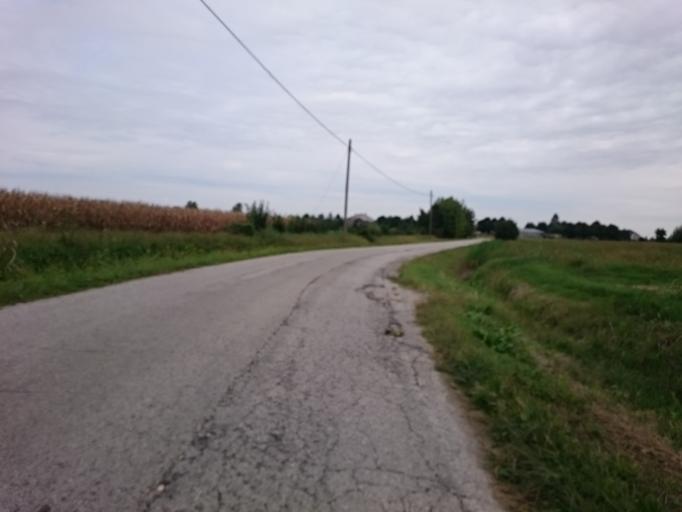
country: IT
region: Veneto
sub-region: Provincia di Vicenza
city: Quinto Vicentino
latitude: 45.5623
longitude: 11.6492
